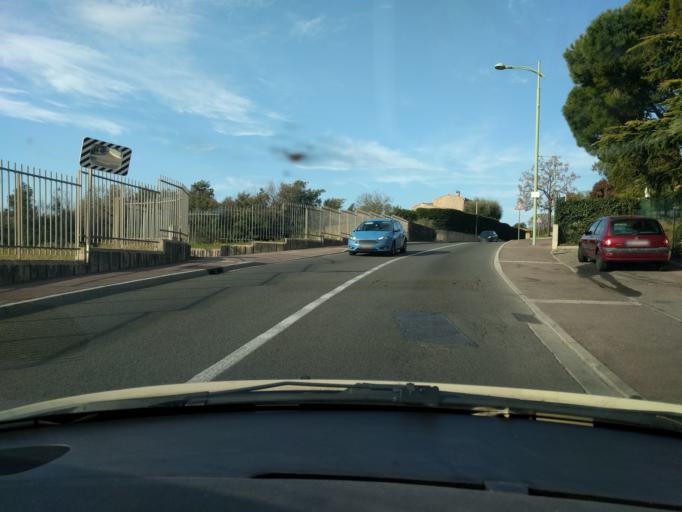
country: FR
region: Provence-Alpes-Cote d'Azur
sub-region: Departement des Alpes-Maritimes
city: Cannes
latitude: 43.5658
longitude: 6.9799
